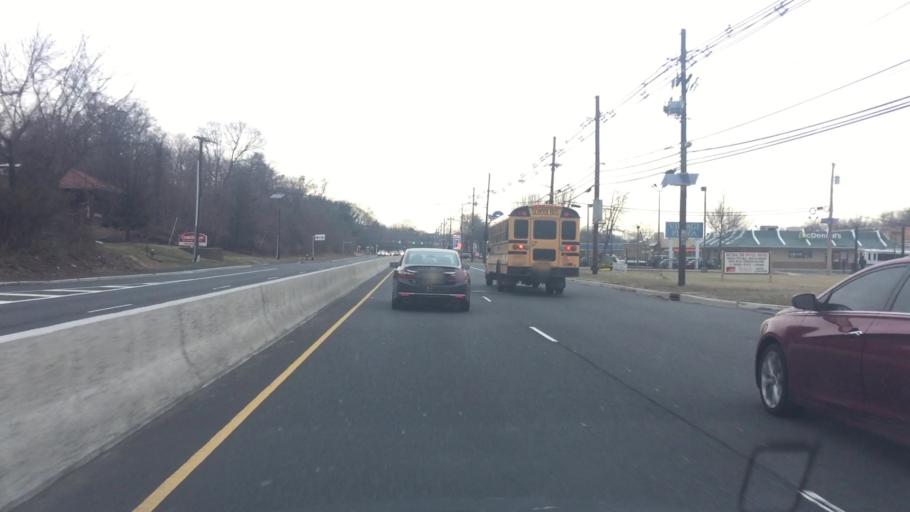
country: US
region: New Jersey
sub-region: Somerset County
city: Somerset
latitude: 40.5148
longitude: -74.4878
